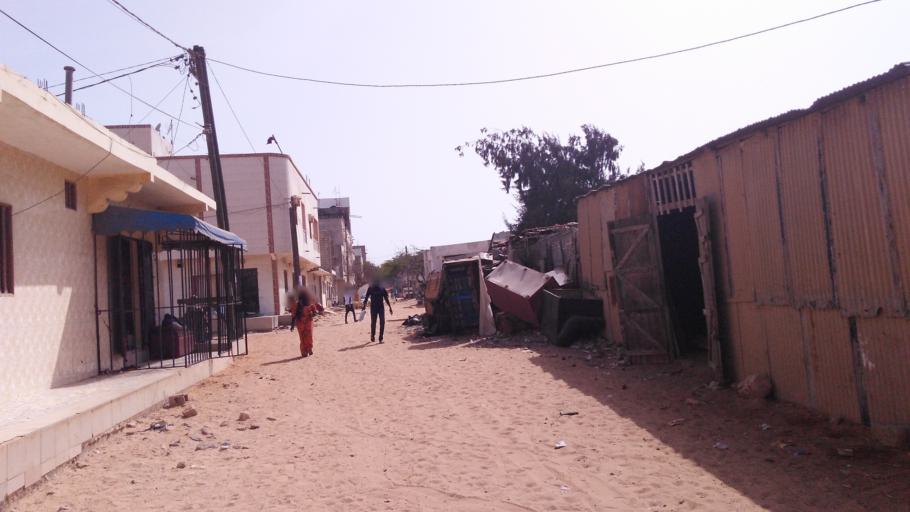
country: SN
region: Dakar
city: Pikine
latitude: 14.7803
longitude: -17.3766
